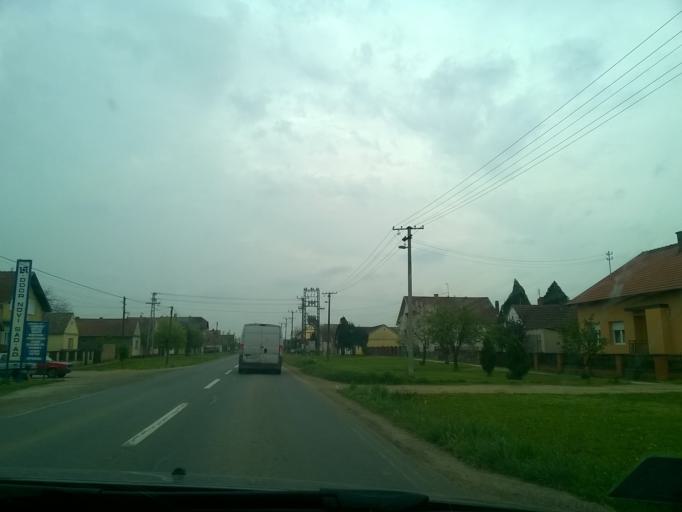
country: RS
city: Platicevo
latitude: 44.8317
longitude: 19.7756
